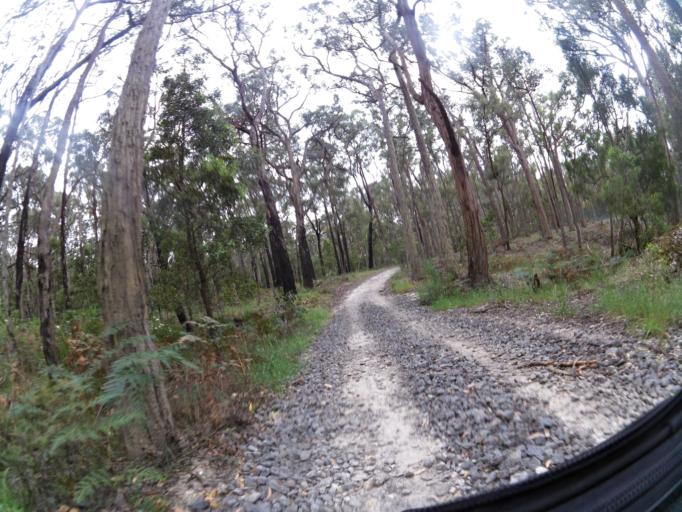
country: AU
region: Victoria
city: Brown Hill
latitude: -37.5177
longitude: 143.9120
